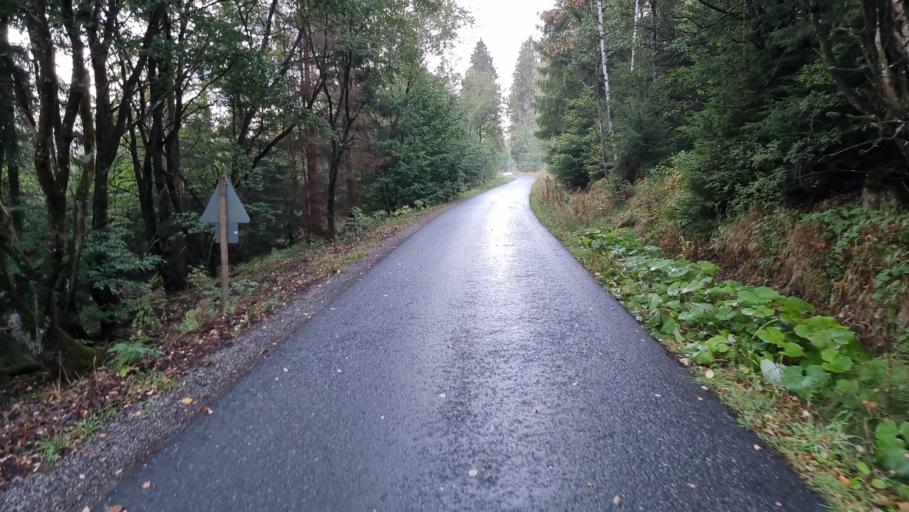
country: DE
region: Lower Saxony
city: Braunlage
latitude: 51.7406
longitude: 10.6104
